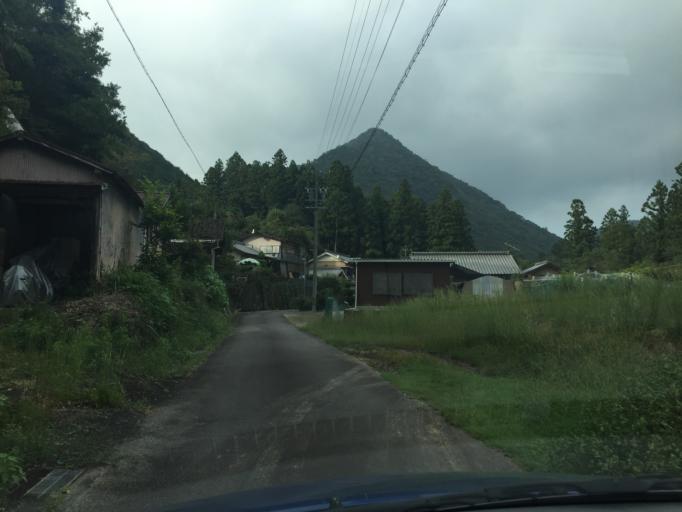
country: JP
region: Aichi
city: Shinshiro
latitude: 34.9776
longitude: 137.6132
